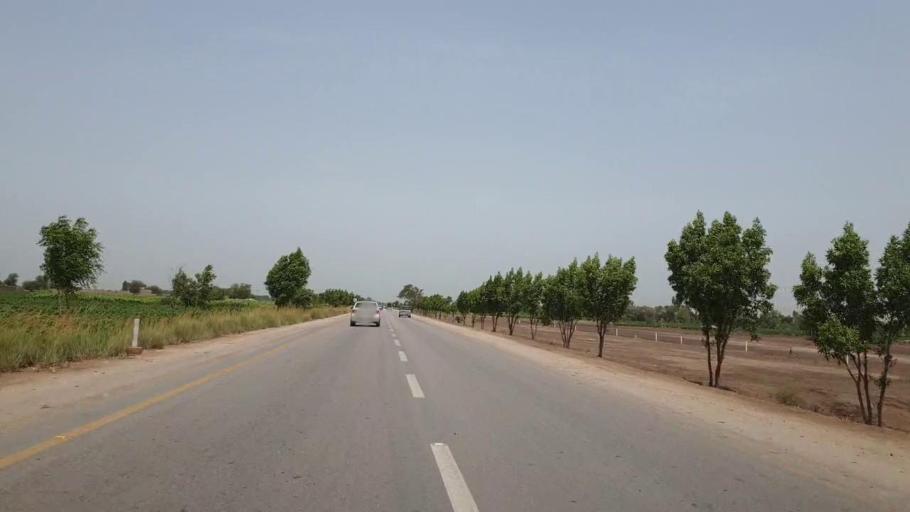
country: PK
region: Sindh
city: Nawabshah
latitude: 26.2327
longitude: 68.4823
